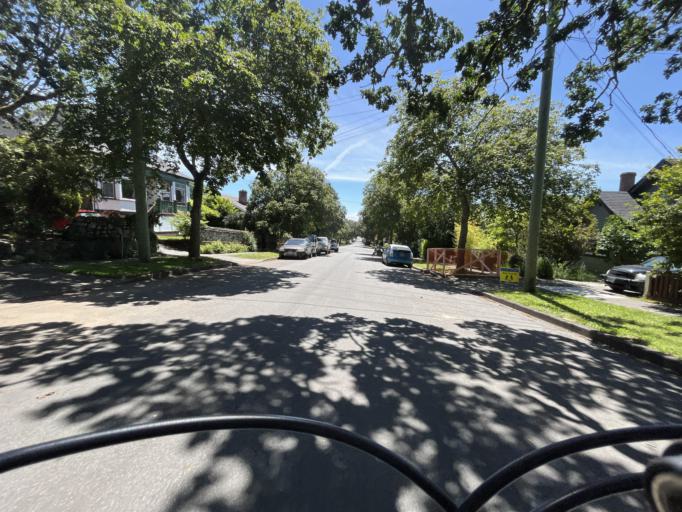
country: CA
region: British Columbia
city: Victoria
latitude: 48.4434
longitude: -123.3576
